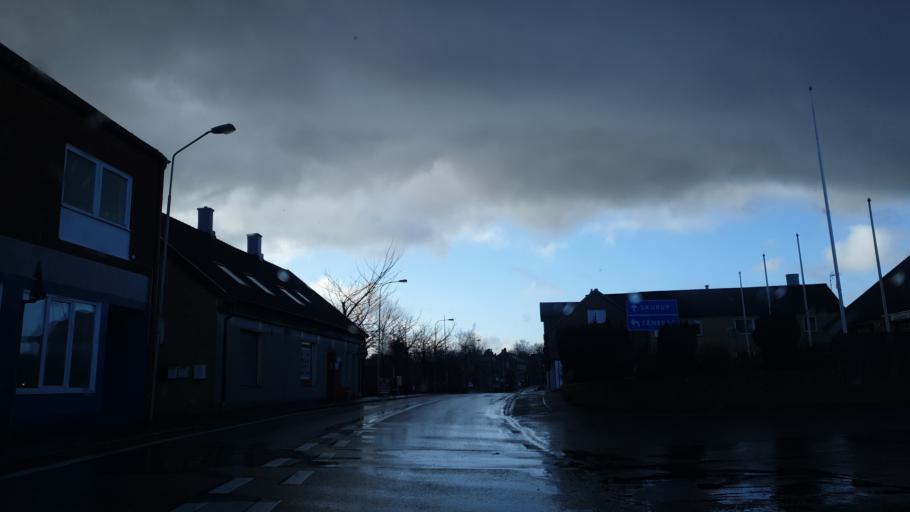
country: SE
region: Skane
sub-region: Skurups Kommun
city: Rydsgard
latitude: 55.4736
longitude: 13.5895
